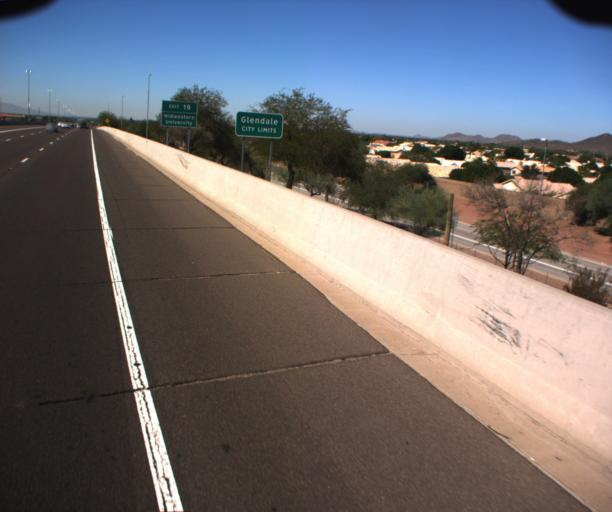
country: US
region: Arizona
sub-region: Maricopa County
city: Peoria
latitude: 33.6685
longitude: -112.1698
